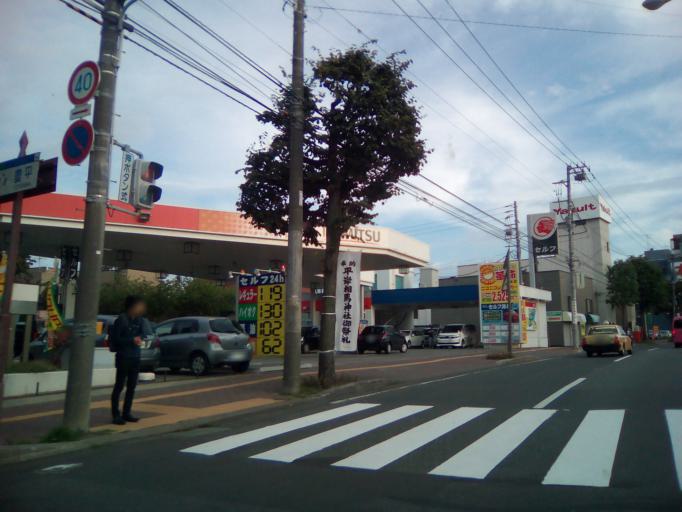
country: JP
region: Hokkaido
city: Sapporo
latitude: 43.0424
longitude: 141.3703
